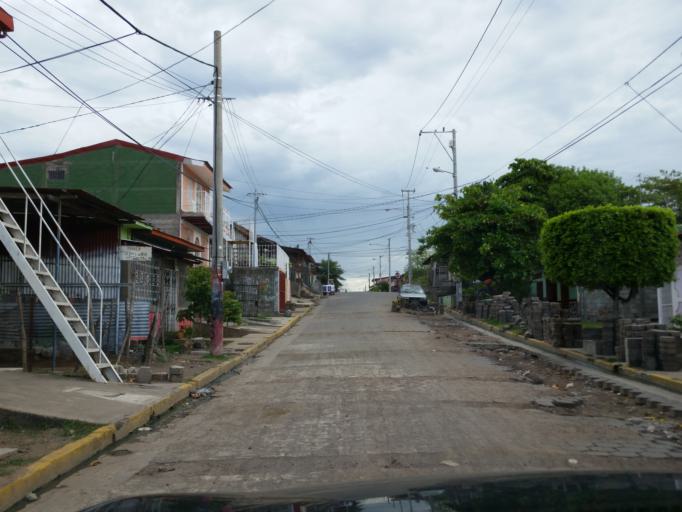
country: NI
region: Granada
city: Granada
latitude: 11.9320
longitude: -85.9471
